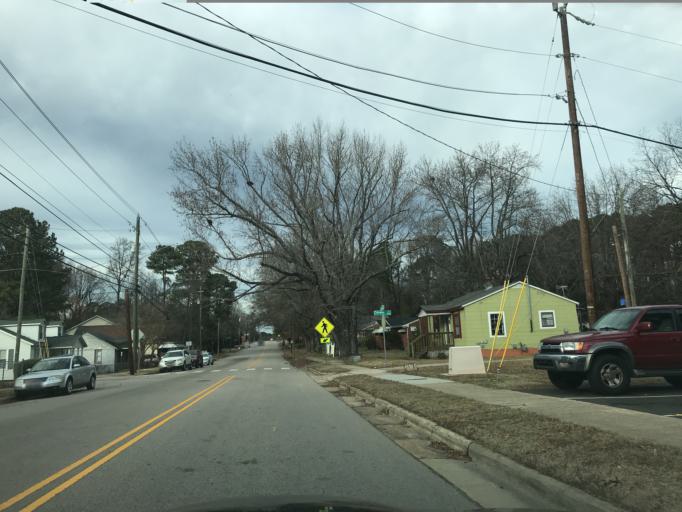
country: US
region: North Carolina
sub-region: Wake County
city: West Raleigh
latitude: 35.7897
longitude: -78.6938
